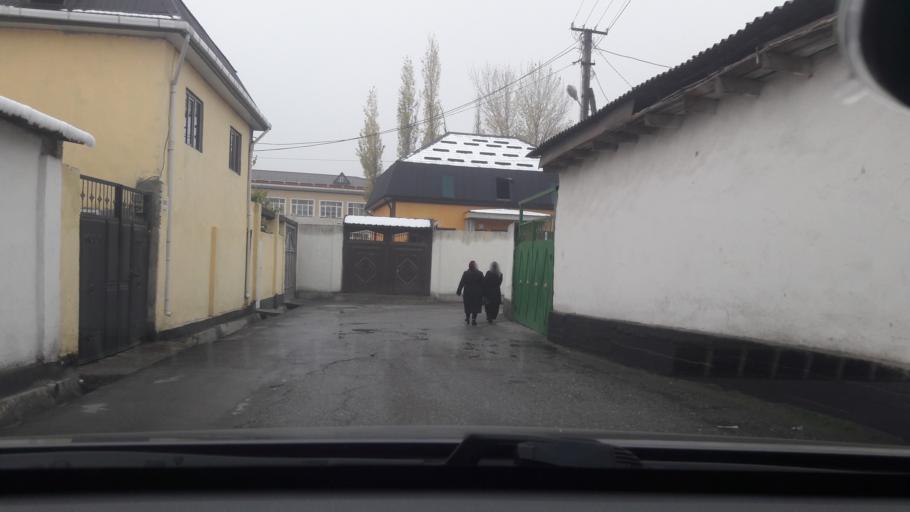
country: TJ
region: Dushanbe
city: Dushanbe
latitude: 38.5891
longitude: 68.7461
